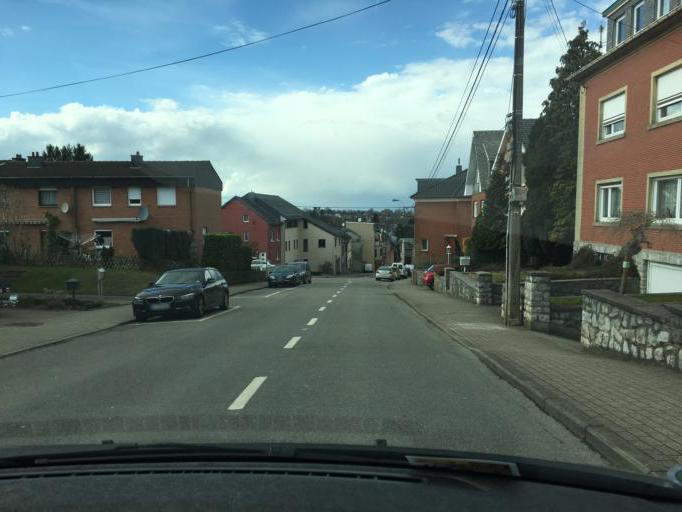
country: BE
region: Wallonia
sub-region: Province de Liege
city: Eupen
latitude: 50.6292
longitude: 6.0395
